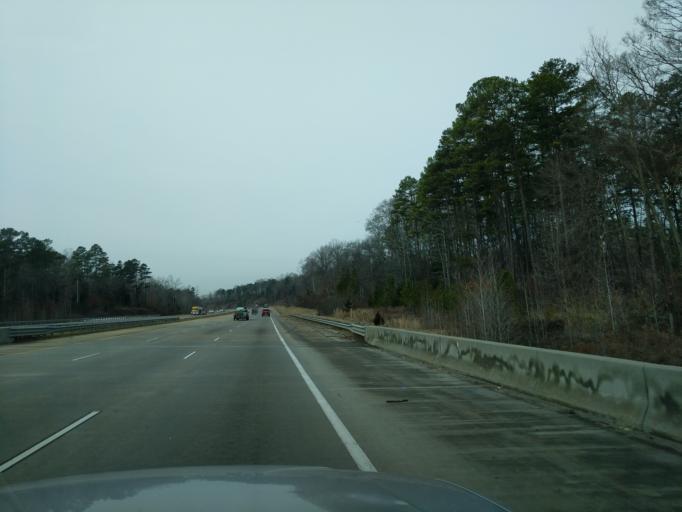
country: US
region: North Carolina
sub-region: Mecklenburg County
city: Huntersville
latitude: 35.3398
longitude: -80.8944
